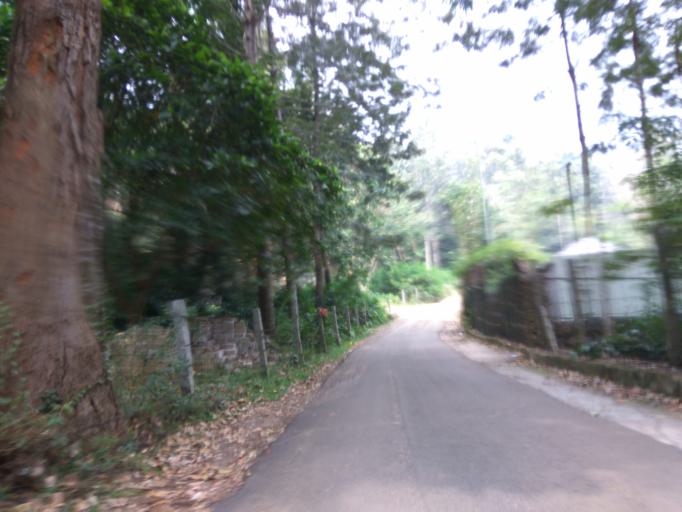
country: IN
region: Tamil Nadu
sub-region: Salem
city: Salem
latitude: 11.7920
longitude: 78.2022
